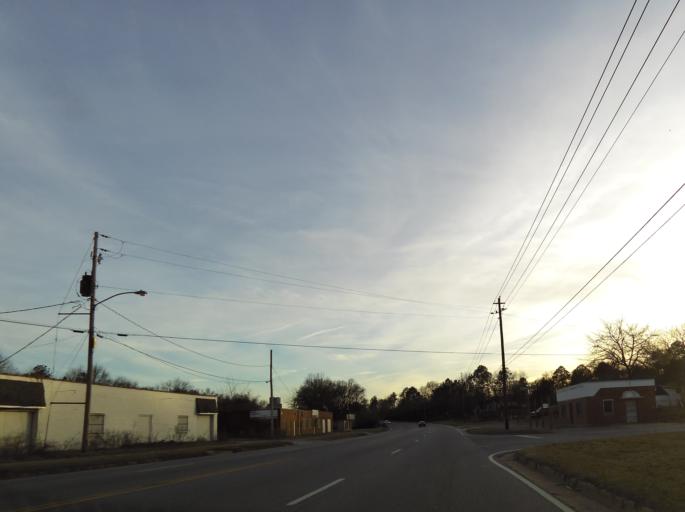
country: US
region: Georgia
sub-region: Bibb County
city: Macon
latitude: 32.7895
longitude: -83.6514
